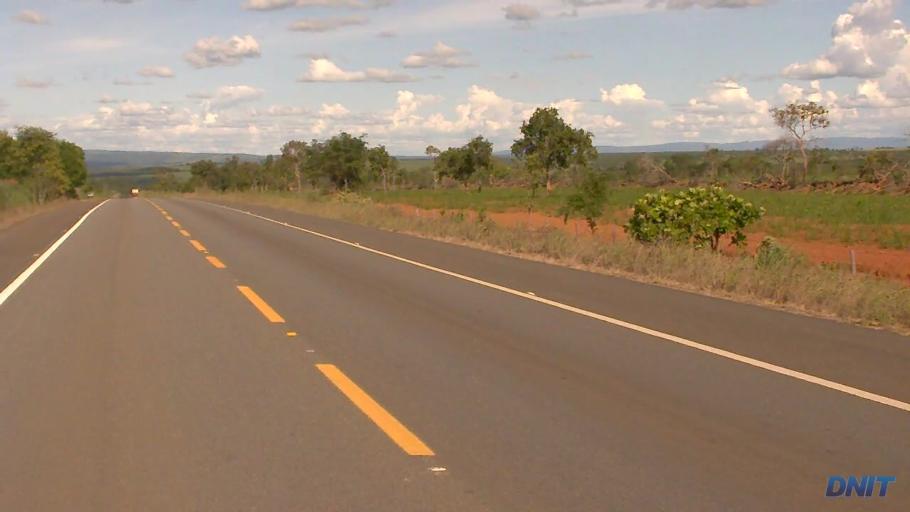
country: BR
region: Goias
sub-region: Barro Alto
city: Barro Alto
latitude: -15.2091
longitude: -48.6870
